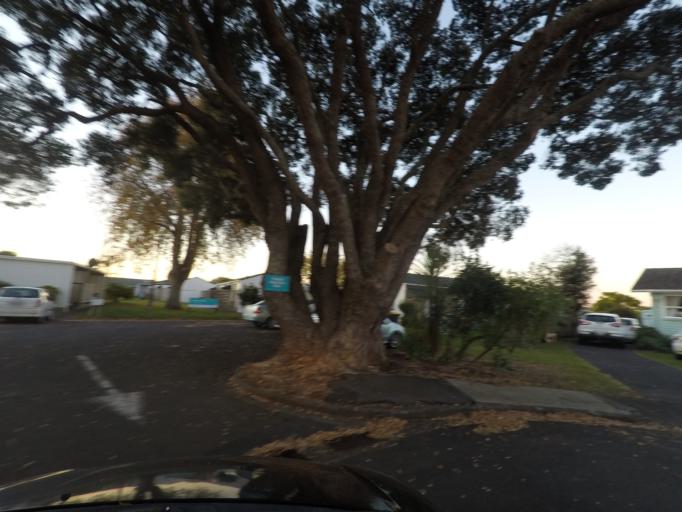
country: NZ
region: Auckland
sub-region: Auckland
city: Rosebank
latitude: -36.8405
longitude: 174.6497
